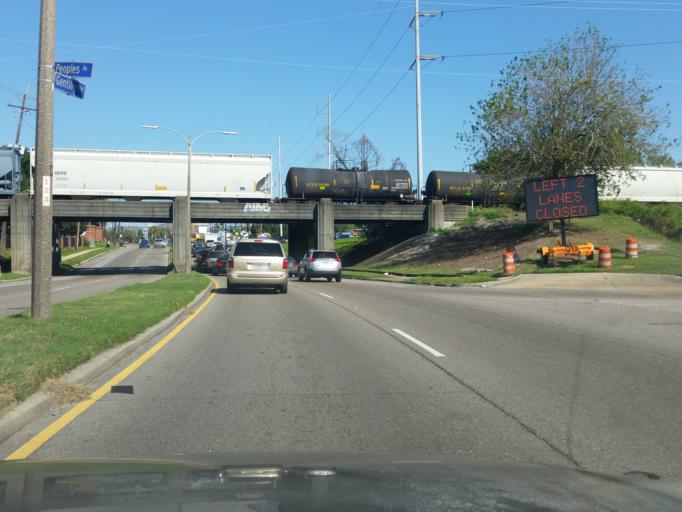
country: US
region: Louisiana
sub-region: Orleans Parish
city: New Orleans
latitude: 30.0027
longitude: -90.0461
